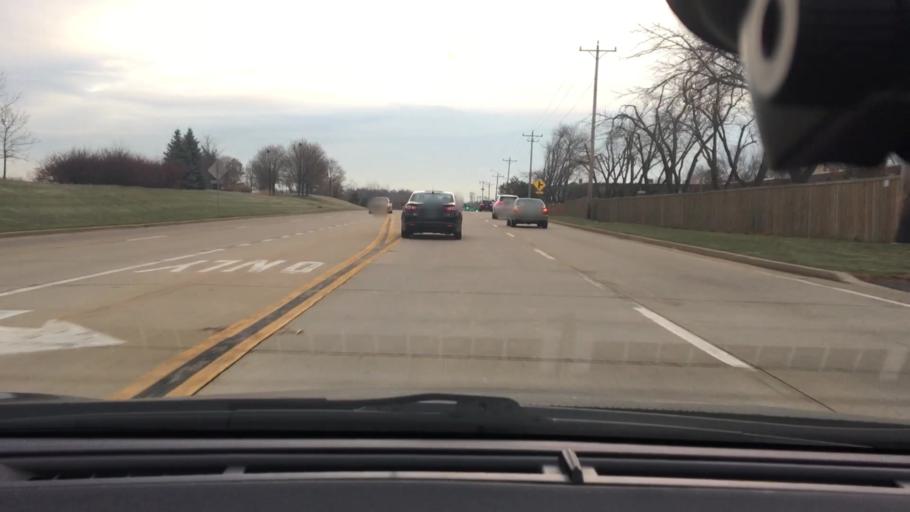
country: US
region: Illinois
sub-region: Lake County
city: Kildeer
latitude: 42.1538
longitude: -88.0488
